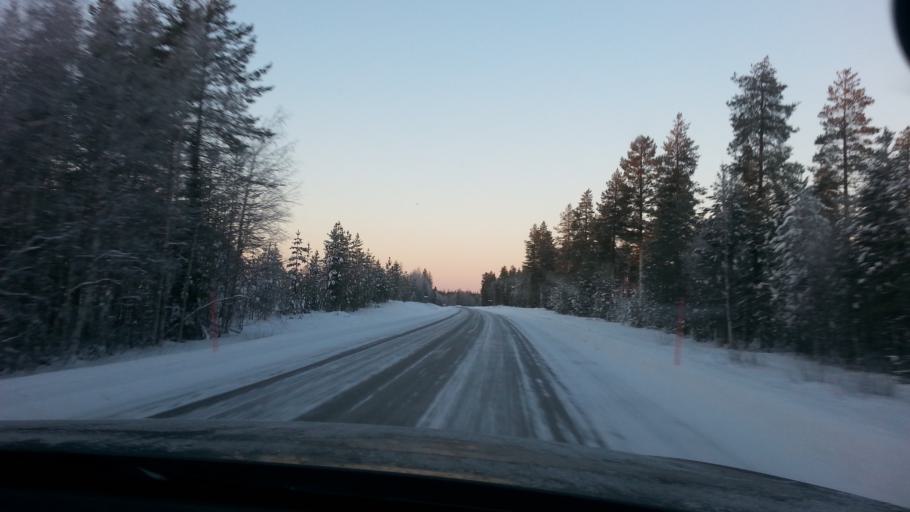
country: FI
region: Lapland
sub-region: Rovaniemi
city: Rovaniemi
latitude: 66.7766
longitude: 25.4551
